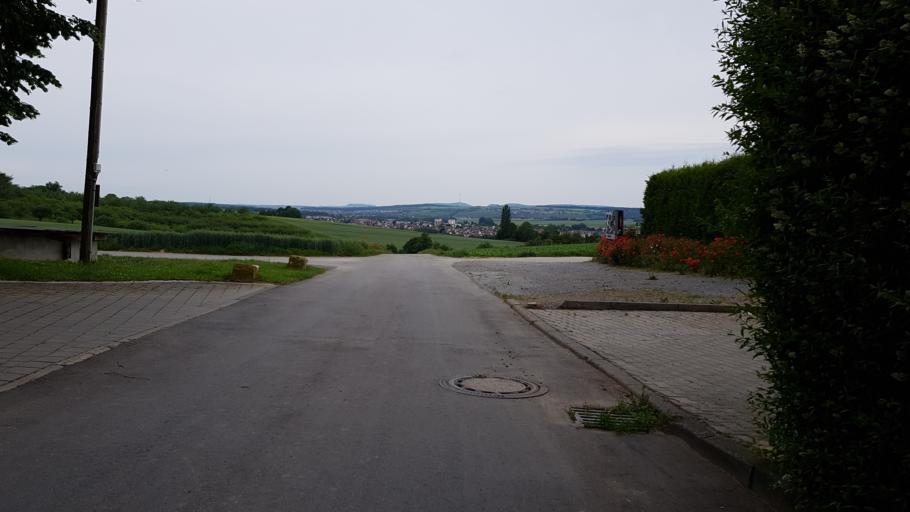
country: DE
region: Baden-Wuerttemberg
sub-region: Regierungsbezirk Stuttgart
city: Steinheim am der Murr
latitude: 48.9564
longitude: 9.2816
